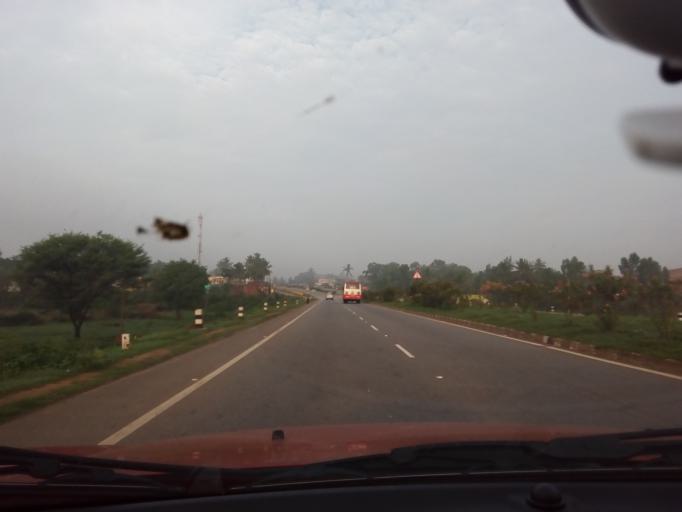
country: IN
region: Karnataka
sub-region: Ramanagara
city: Magadi
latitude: 13.0675
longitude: 77.1763
